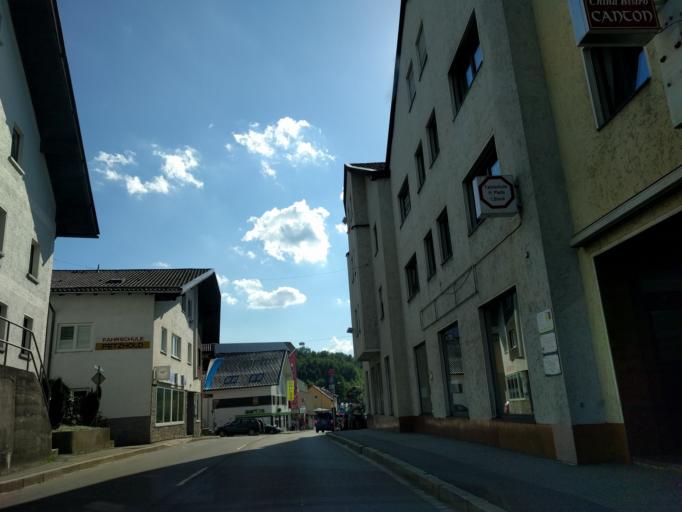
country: DE
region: Bavaria
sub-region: Lower Bavaria
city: Regen
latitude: 48.9693
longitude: 13.1306
